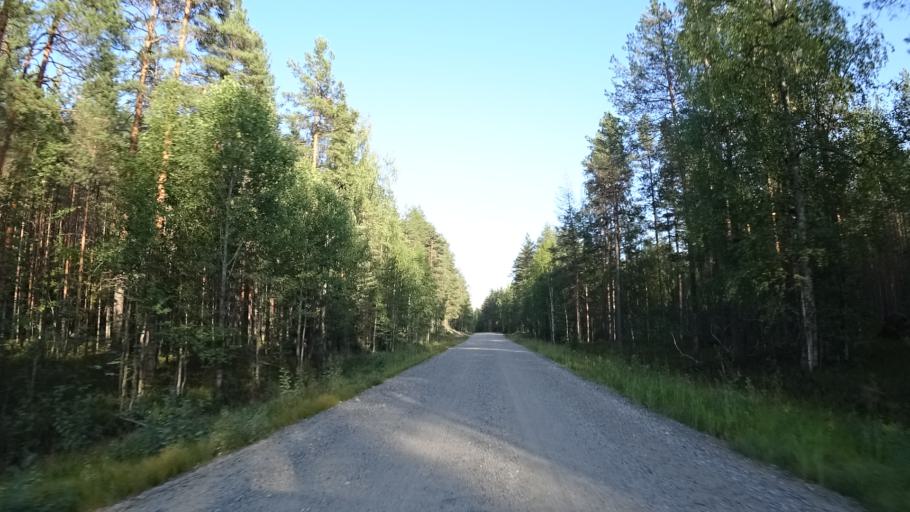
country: FI
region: North Karelia
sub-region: Joensuu
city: Ilomantsi
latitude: 63.1392
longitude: 30.6940
